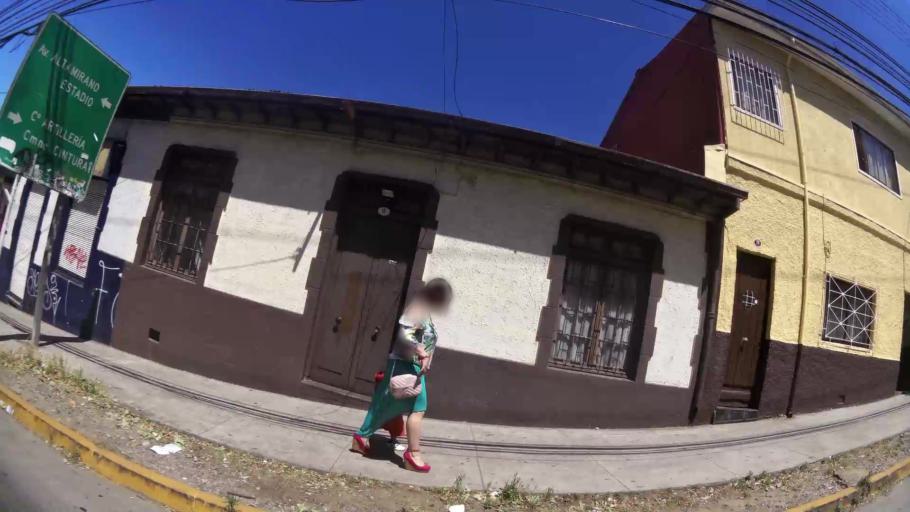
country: CL
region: Valparaiso
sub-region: Provincia de Valparaiso
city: Valparaiso
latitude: -33.0302
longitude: -71.6366
